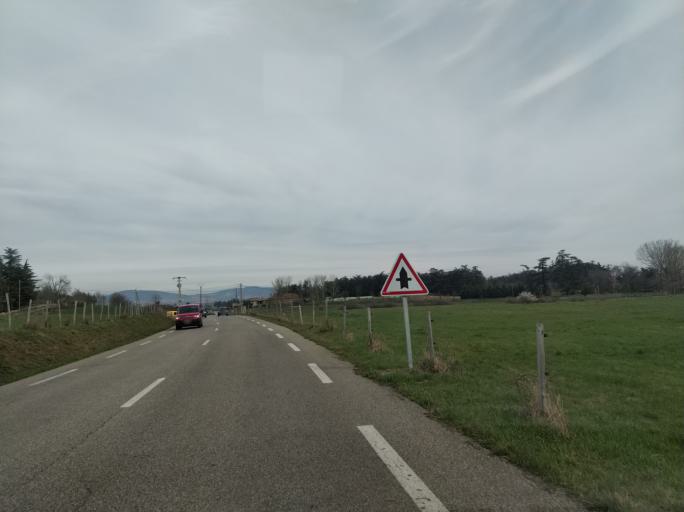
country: FR
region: Rhone-Alpes
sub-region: Departement de l'Ardeche
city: Roiffieux
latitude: 45.2080
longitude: 4.6586
